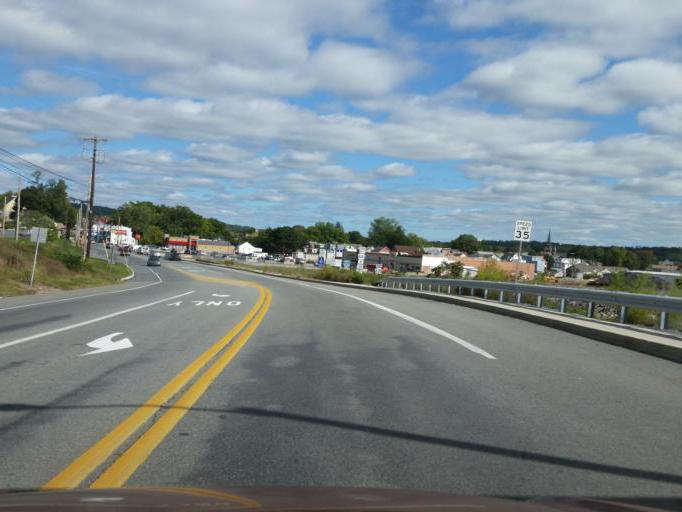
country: US
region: Pennsylvania
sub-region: Dauphin County
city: Middletown
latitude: 40.1967
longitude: -76.7390
